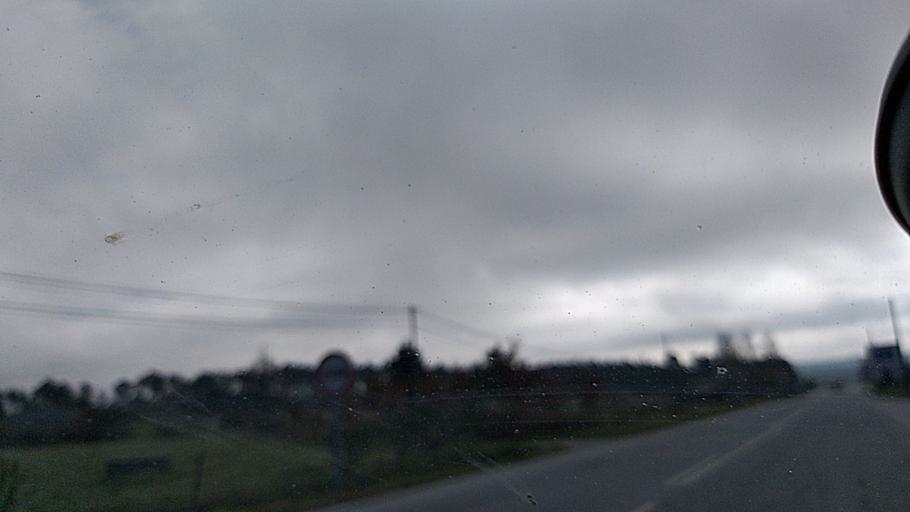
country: PT
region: Guarda
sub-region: Aguiar da Beira
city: Aguiar da Beira
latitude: 40.7914
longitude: -7.5100
